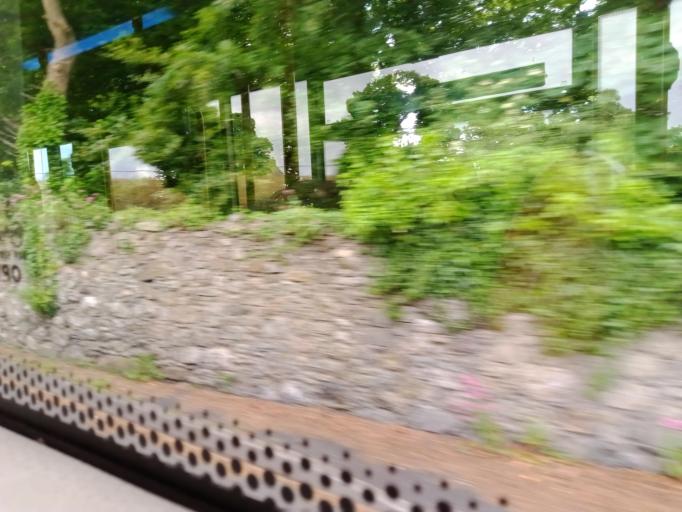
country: GB
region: Wales
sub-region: Anglesey
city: Menai Bridge
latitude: 53.2373
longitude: -4.1532
